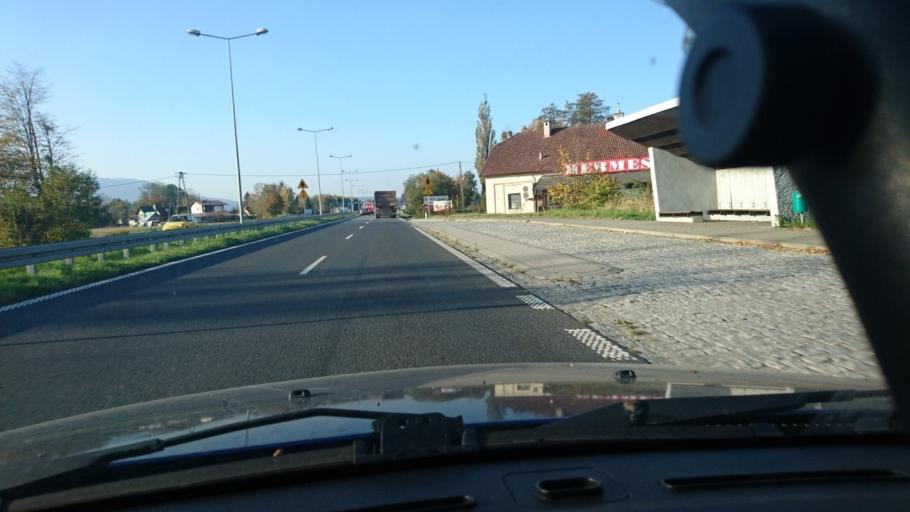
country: PL
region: Silesian Voivodeship
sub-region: Powiat cieszynski
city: Gorki Wielkie
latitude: 49.7603
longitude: 18.8064
